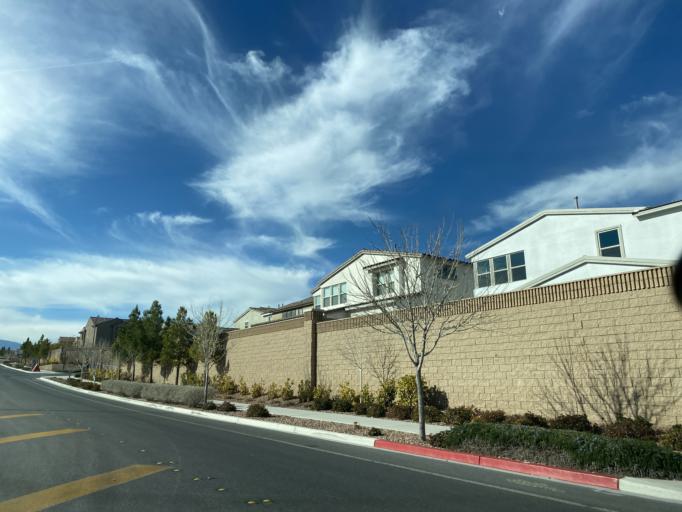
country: US
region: Nevada
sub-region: Clark County
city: Summerlin South
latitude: 36.3104
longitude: -115.3099
